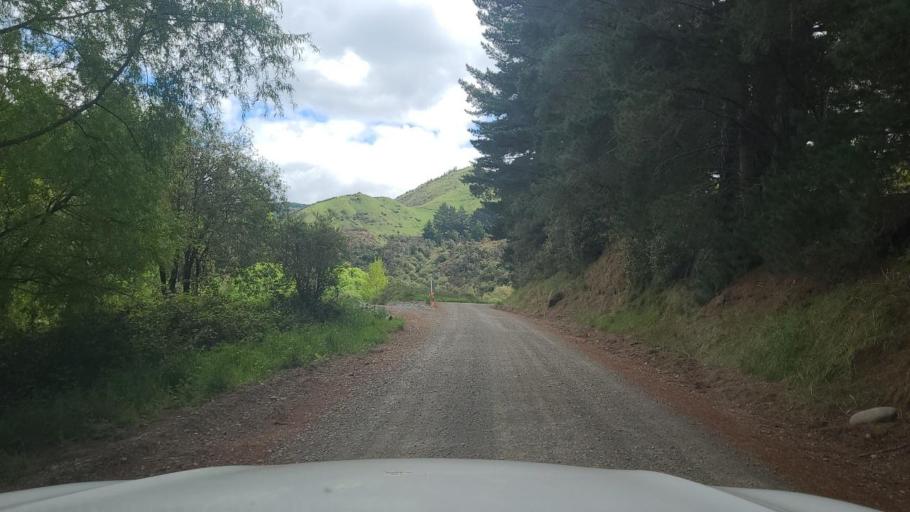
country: NZ
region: Hawke's Bay
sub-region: Napier City
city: Taradale
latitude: -39.1952
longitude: 176.6166
